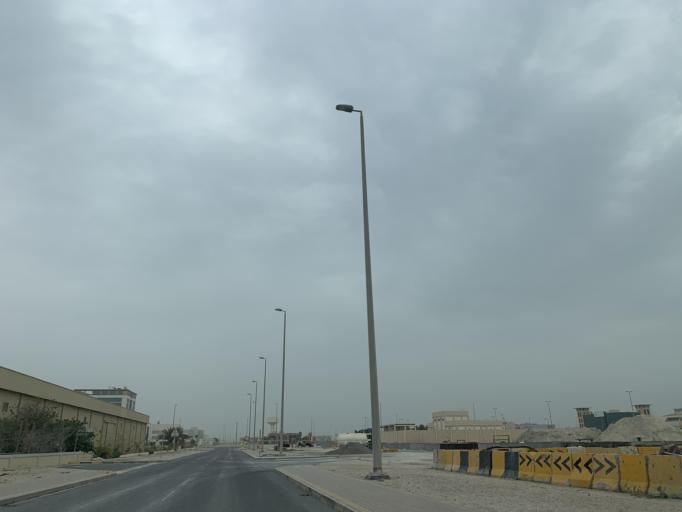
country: BH
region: Muharraq
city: Al Hadd
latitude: 26.2222
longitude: 50.6711
